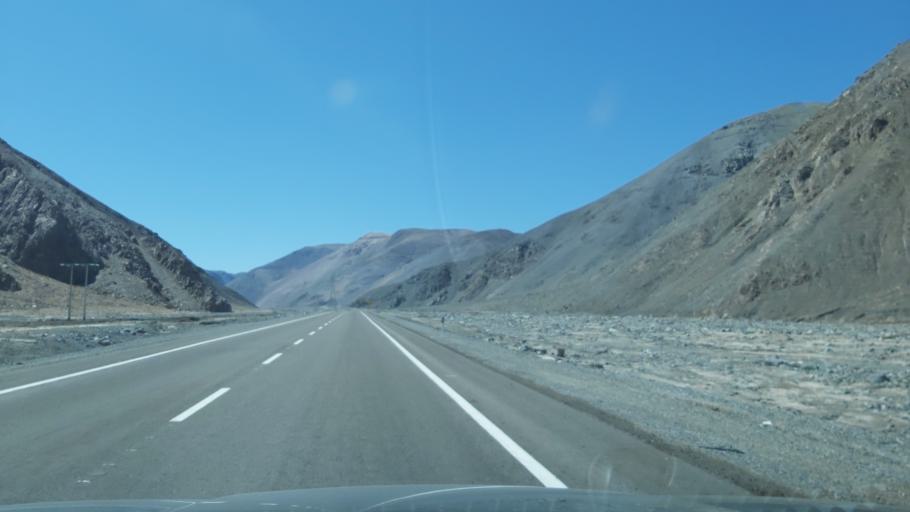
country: CL
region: Atacama
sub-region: Provincia de Chanaral
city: Diego de Almagro
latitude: -26.3508
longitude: -69.7367
